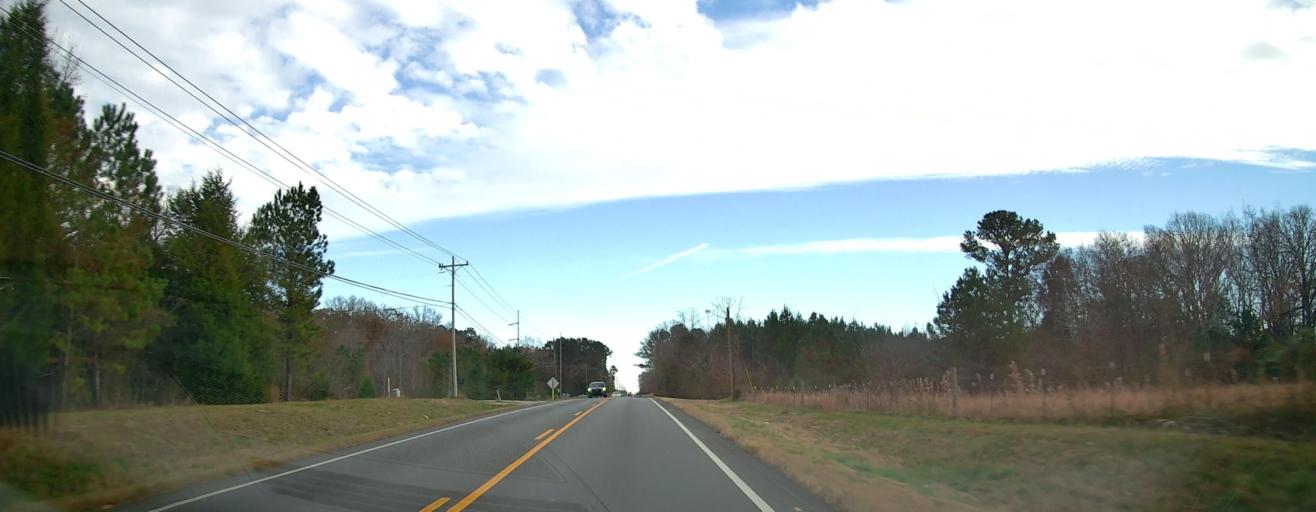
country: US
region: Alabama
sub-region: Morgan County
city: Priceville
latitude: 34.4520
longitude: -86.7655
